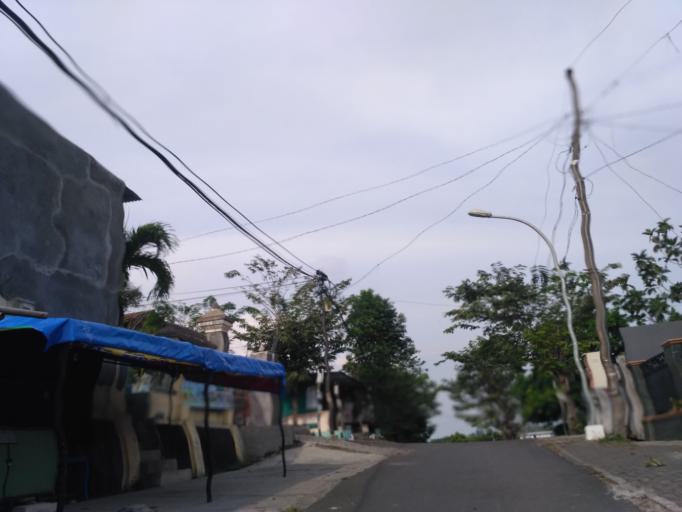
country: ID
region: Central Java
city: Semarang
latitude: -7.0189
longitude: 110.4465
